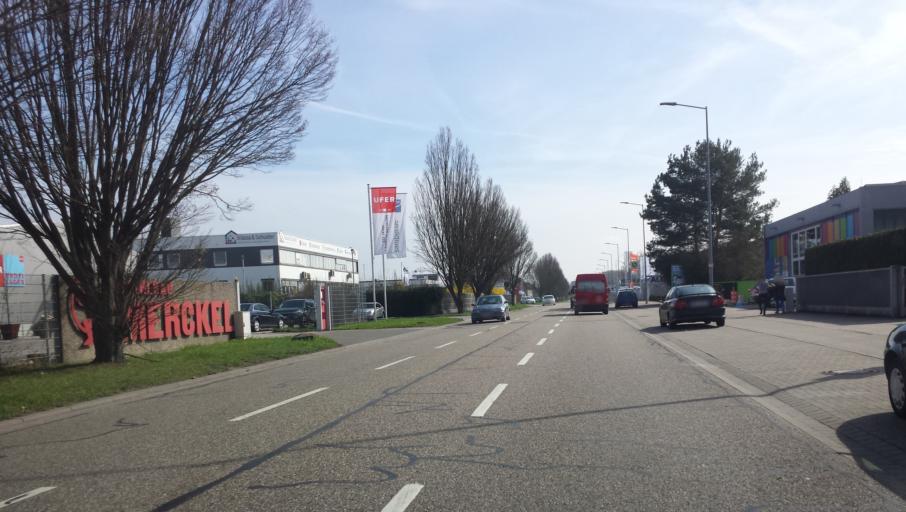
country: DE
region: Rheinland-Pfalz
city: Speyer
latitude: 49.3078
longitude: 8.4454
